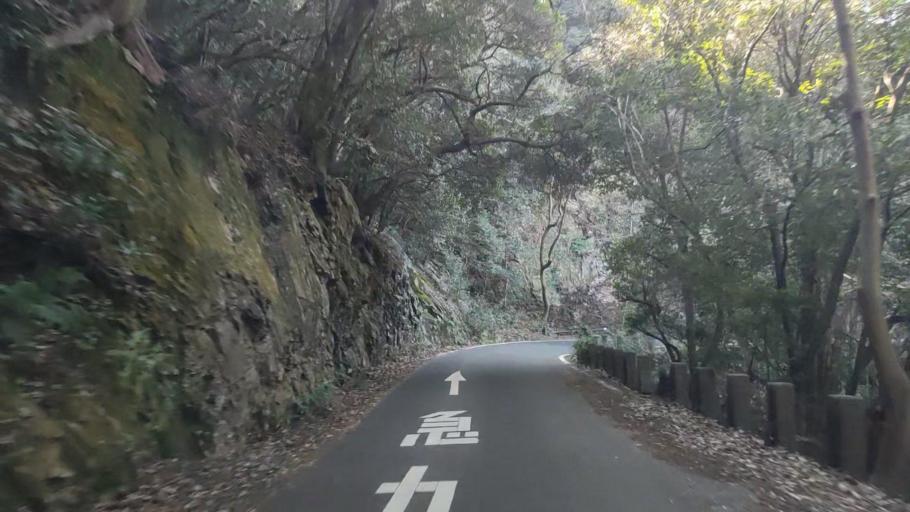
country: JP
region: Gifu
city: Gifu-shi
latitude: 35.4268
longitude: 136.7724
